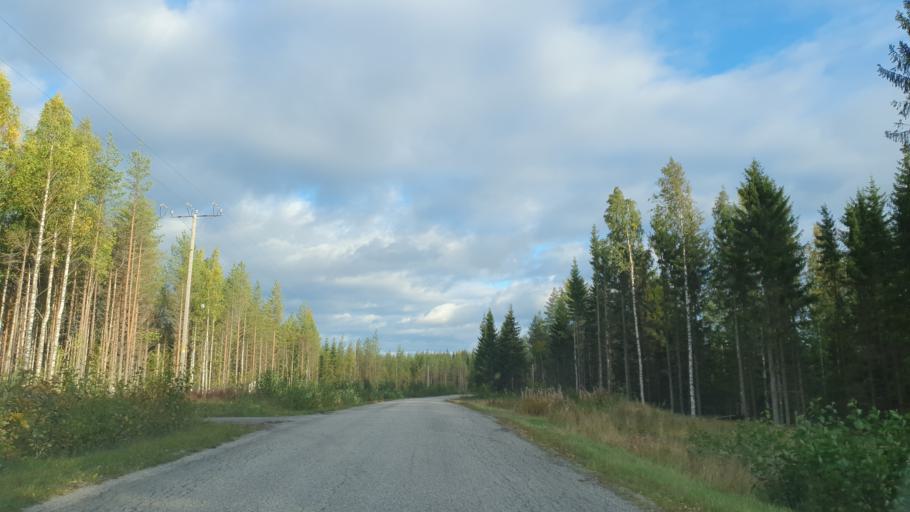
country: FI
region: Kainuu
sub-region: Kehys-Kainuu
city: Kuhmo
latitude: 63.9252
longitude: 30.0344
